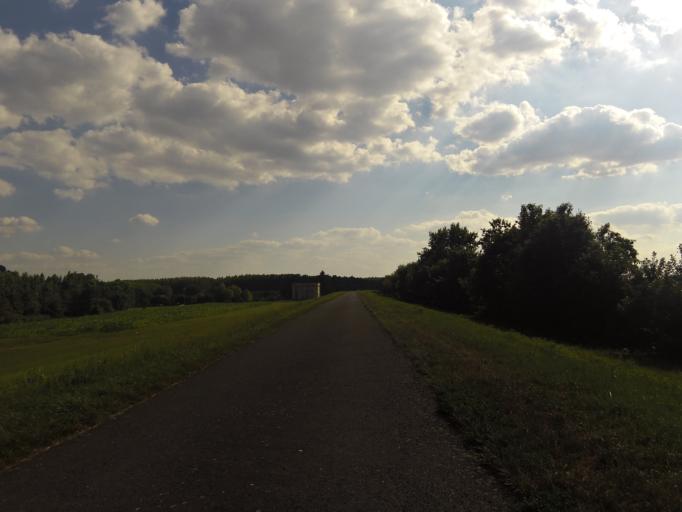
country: HU
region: Jasz-Nagykun-Szolnok
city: Abadszalok
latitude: 47.5272
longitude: 20.6073
